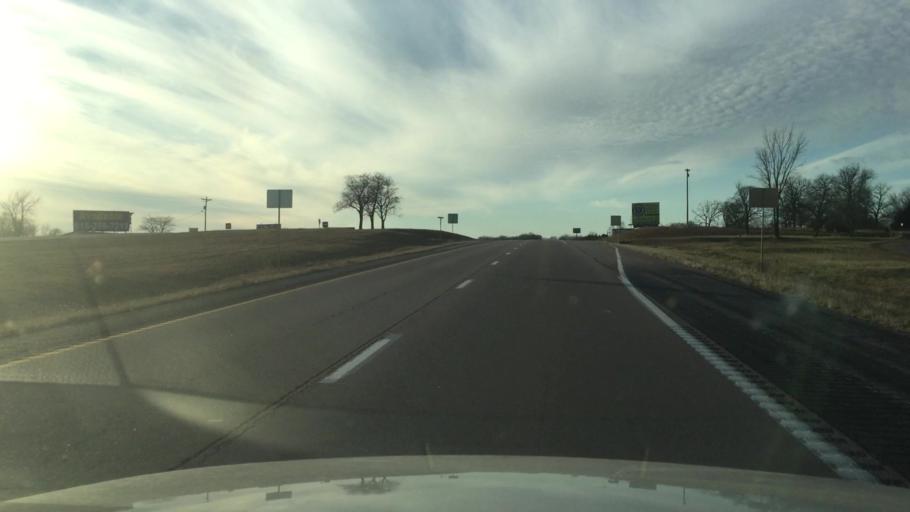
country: US
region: Missouri
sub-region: Miller County
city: Eldon
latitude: 38.3679
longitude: -92.5033
